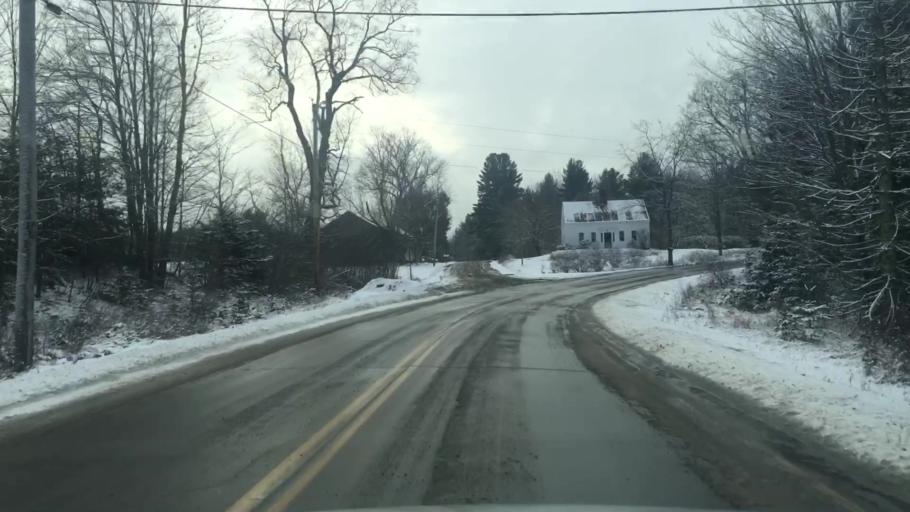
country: US
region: Maine
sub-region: Waldo County
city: Searsmont
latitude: 44.3618
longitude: -69.1500
